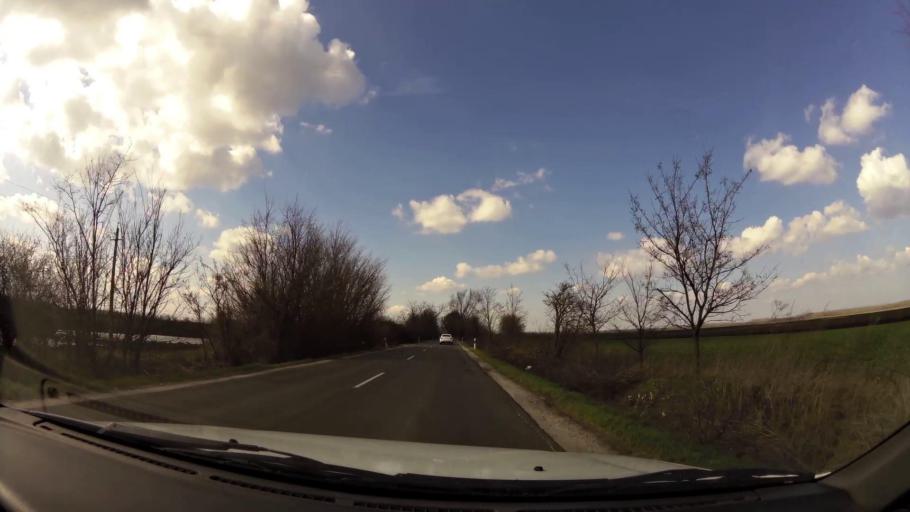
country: HU
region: Pest
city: Szentmartonkata
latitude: 47.4374
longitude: 19.7245
